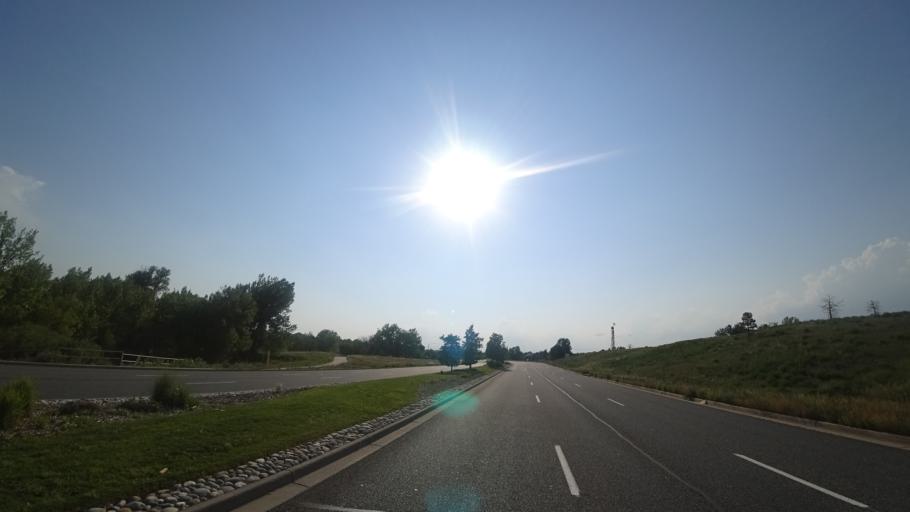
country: US
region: Colorado
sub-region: Douglas County
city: Parker
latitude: 39.5953
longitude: -104.7408
